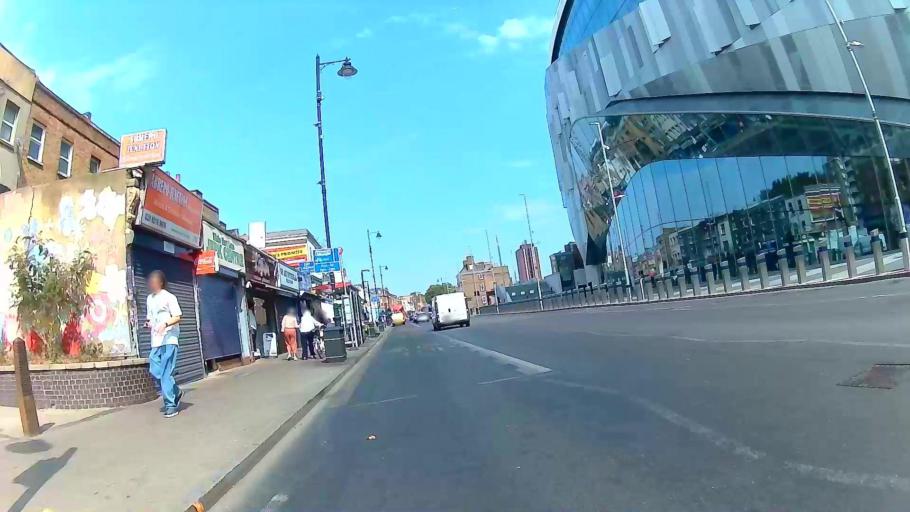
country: GB
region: England
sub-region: Greater London
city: Harringay
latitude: 51.6037
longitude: -0.0680
